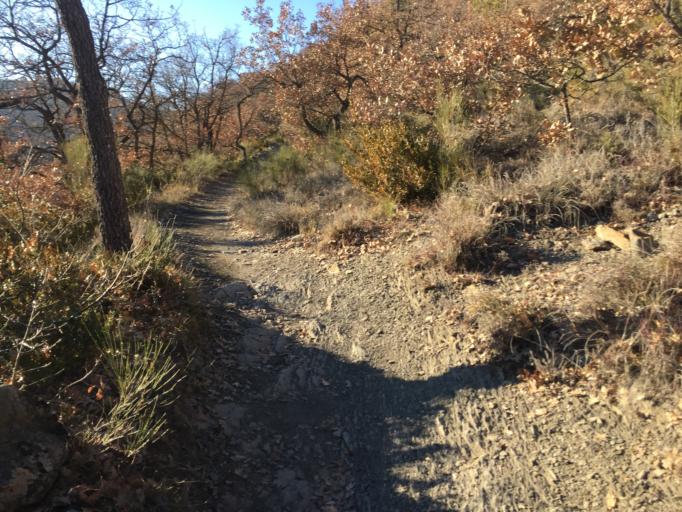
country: FR
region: Provence-Alpes-Cote d'Azur
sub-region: Departement des Alpes-de-Haute-Provence
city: Digne-les-Bains
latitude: 44.0814
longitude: 6.2665
